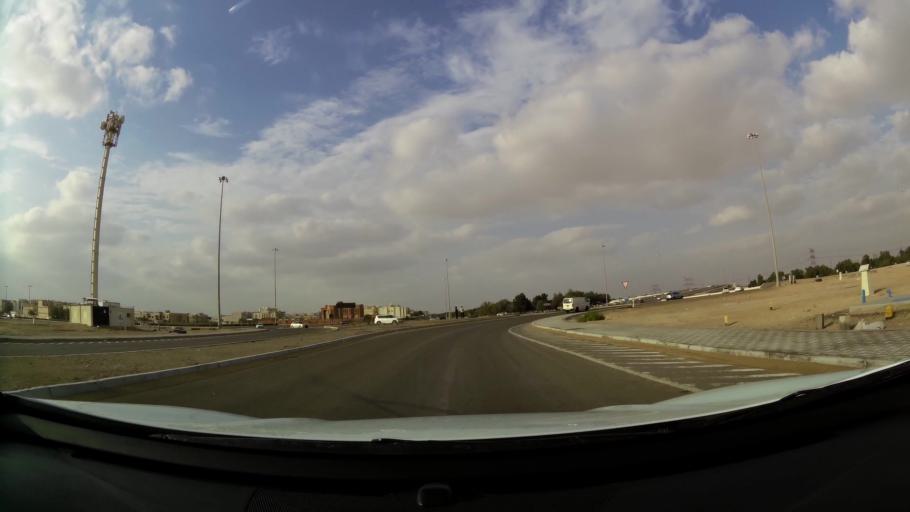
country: AE
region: Abu Dhabi
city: Abu Dhabi
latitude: 24.3471
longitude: 54.5663
